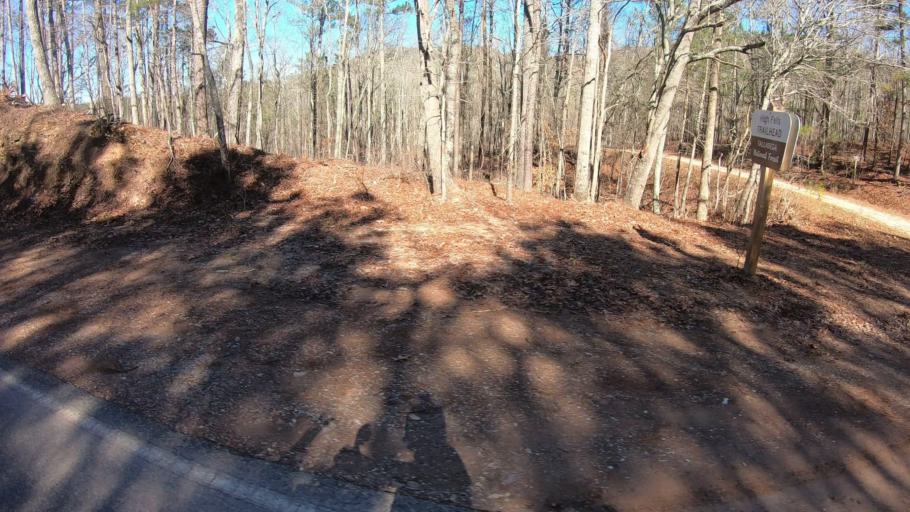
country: US
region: Alabama
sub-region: Clay County
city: Ashland
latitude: 33.3670
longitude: -85.8428
